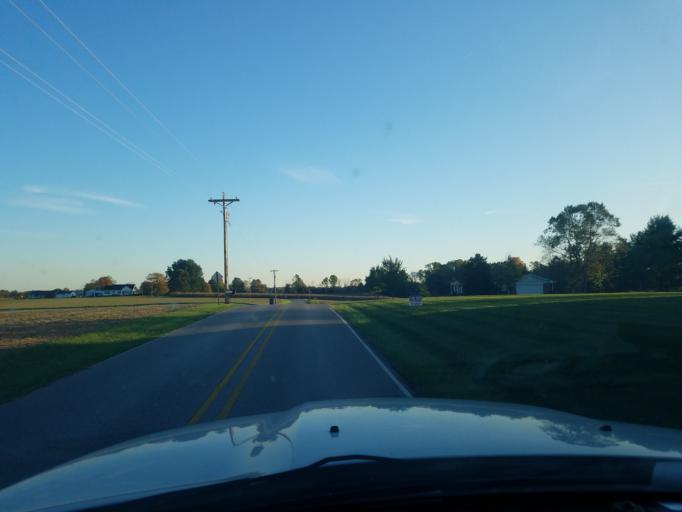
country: US
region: Indiana
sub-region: Floyd County
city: Galena
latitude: 38.4064
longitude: -85.9109
